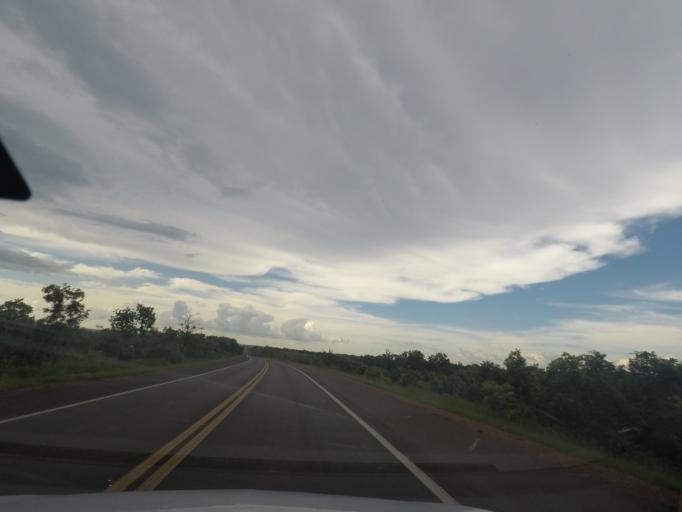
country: BR
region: Minas Gerais
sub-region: Prata
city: Prata
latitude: -19.5786
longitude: -48.8249
